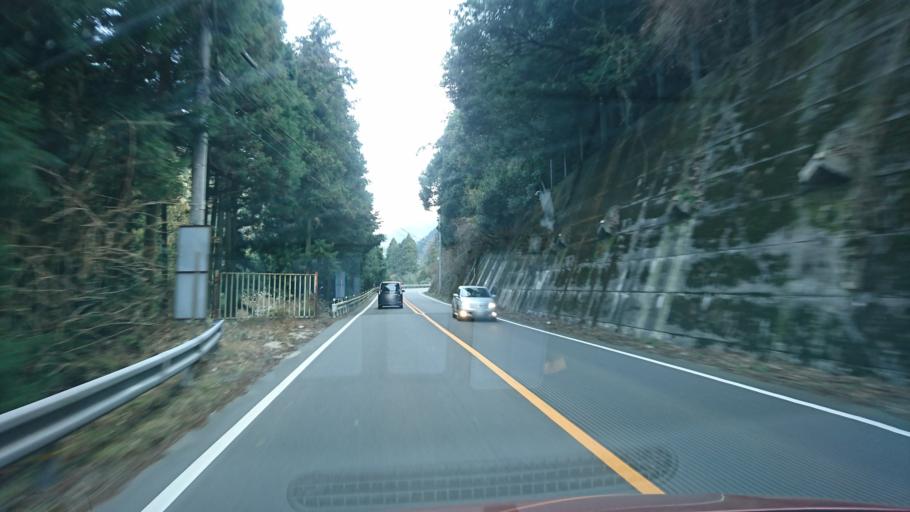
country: JP
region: Ehime
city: Hojo
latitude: 33.9662
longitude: 132.9053
